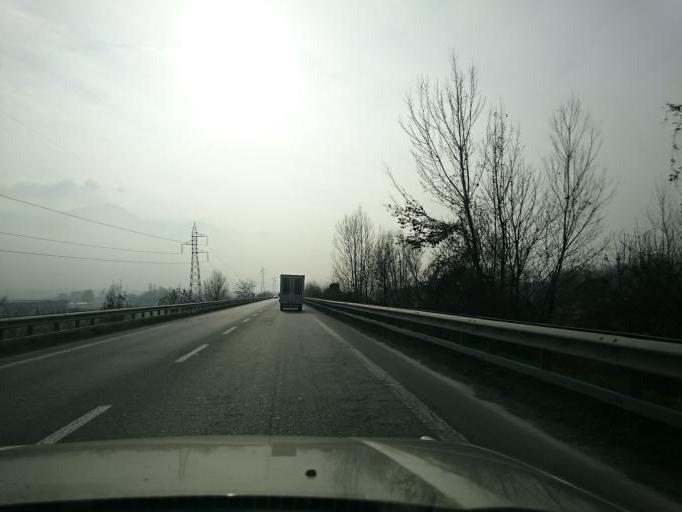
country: IT
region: Lombardy
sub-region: Provincia di Brescia
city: Artogne
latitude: 45.8677
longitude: 10.1590
